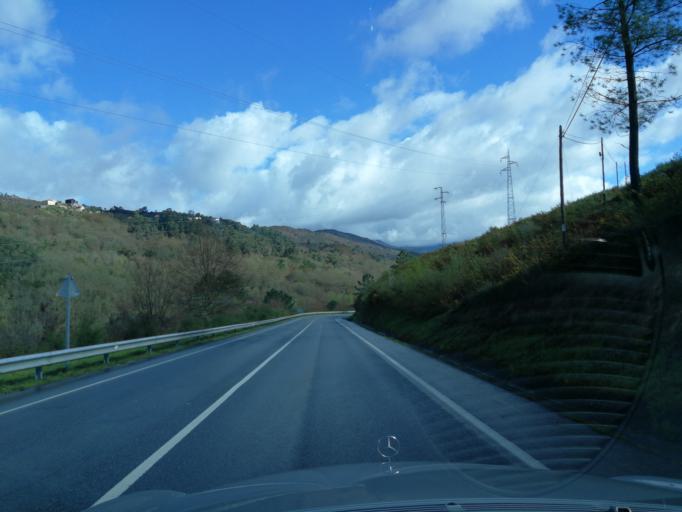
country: PT
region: Braga
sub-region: Terras de Bouro
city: Antas
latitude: 41.8251
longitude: -8.3114
